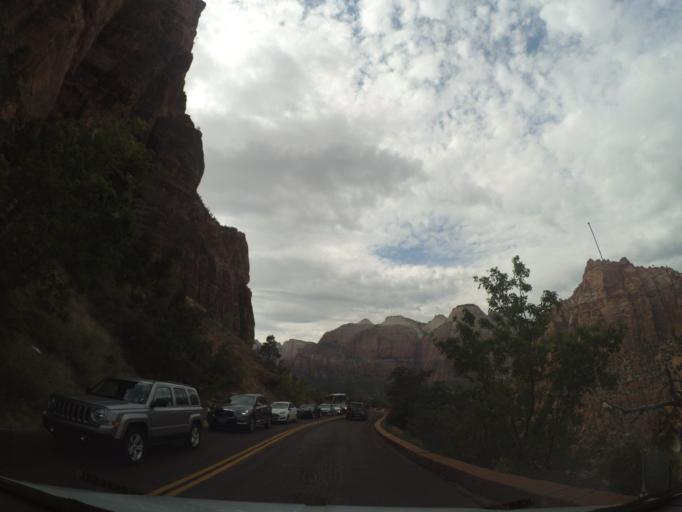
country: US
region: Utah
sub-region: Washington County
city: Hildale
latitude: 37.2123
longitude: -112.9609
